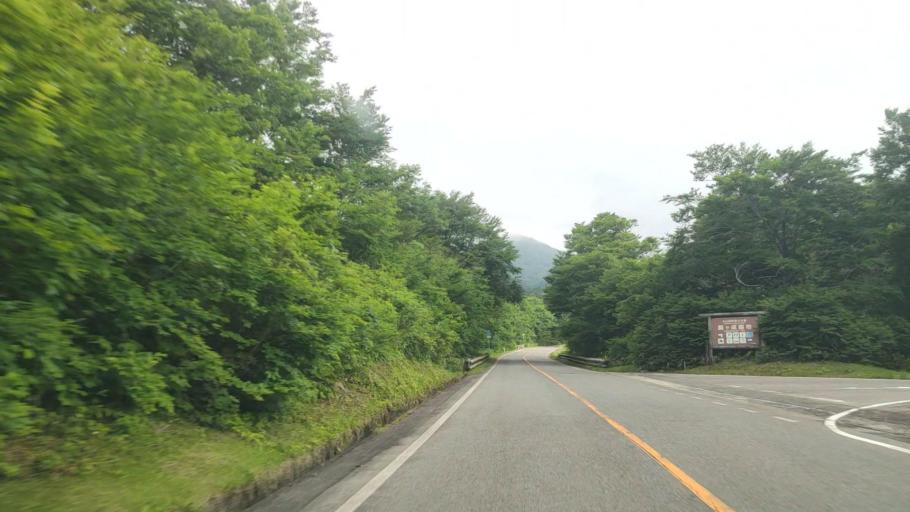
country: JP
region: Tottori
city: Kurayoshi
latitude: 35.3433
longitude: 133.5892
